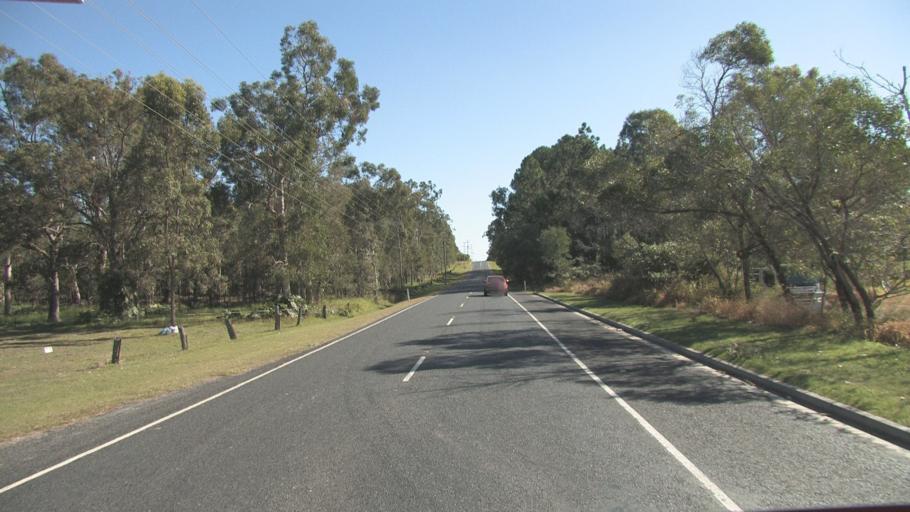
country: AU
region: Queensland
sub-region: Logan
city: Logan Reserve
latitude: -27.7207
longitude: 153.0808
